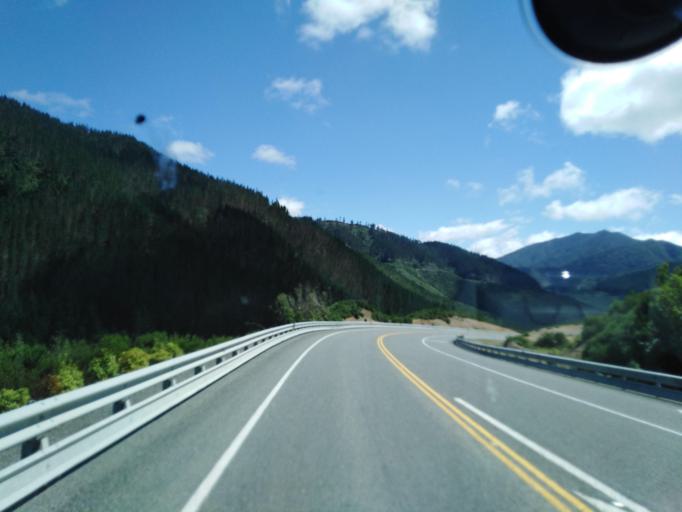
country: NZ
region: Nelson
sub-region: Nelson City
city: Nelson
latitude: -41.1893
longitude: 173.5539
